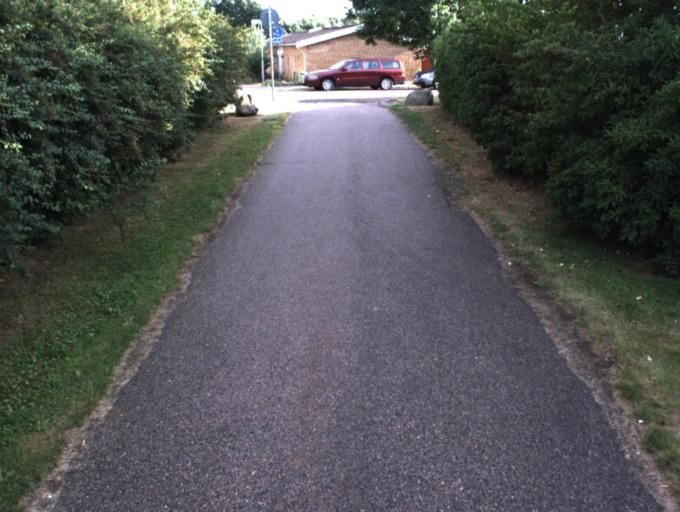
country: SE
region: Skane
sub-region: Helsingborg
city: Rydeback
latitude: 56.0223
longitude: 12.7579
